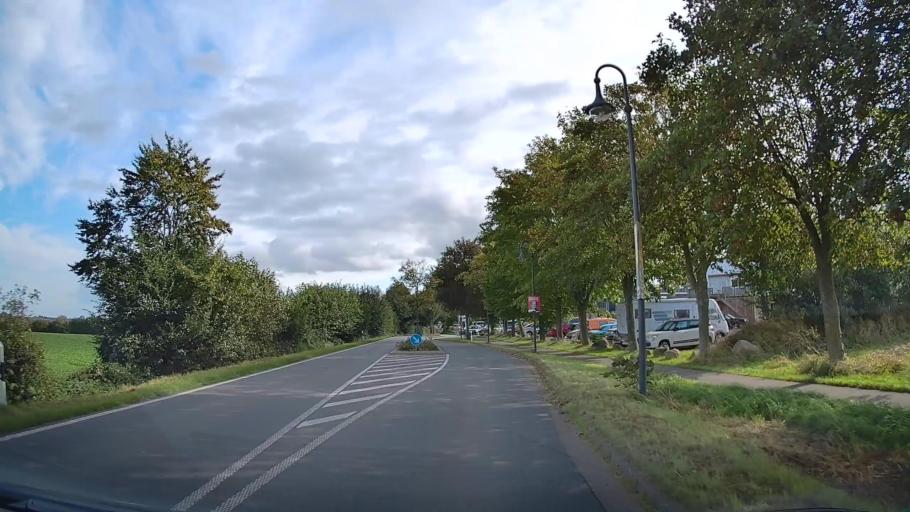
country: DE
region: Schleswig-Holstein
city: Ringsberg
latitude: 54.8110
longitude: 9.5951
